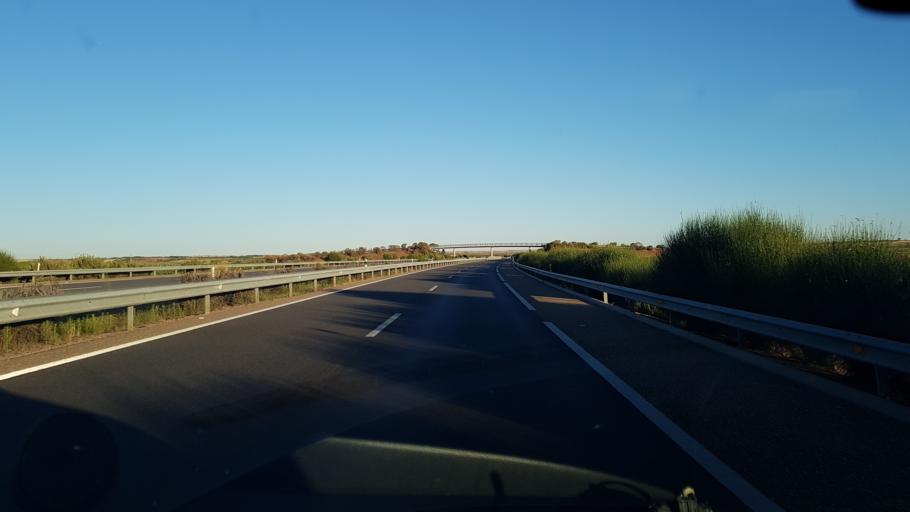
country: ES
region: Castille and Leon
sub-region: Provincia de Valladolid
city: Pedrosa del Rey
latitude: 41.5226
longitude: -5.2343
